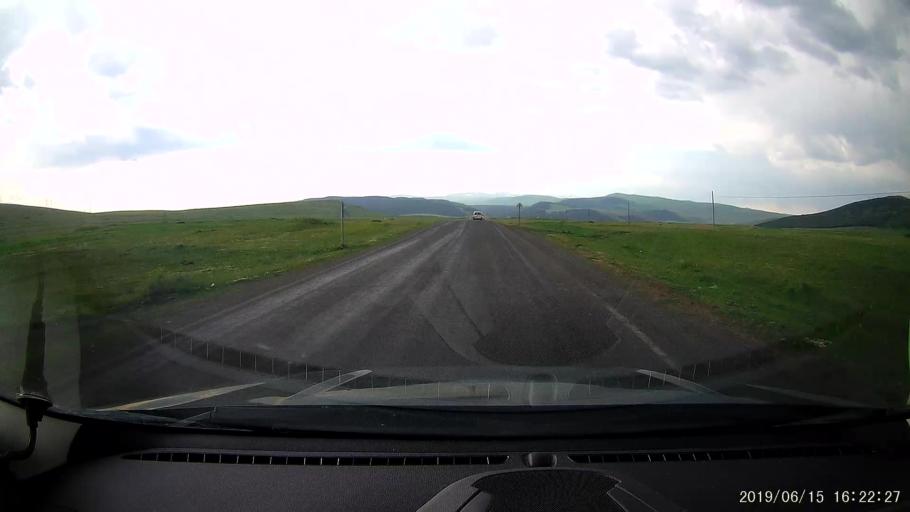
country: TR
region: Ardahan
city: Hanak
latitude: 41.1879
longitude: 42.8509
